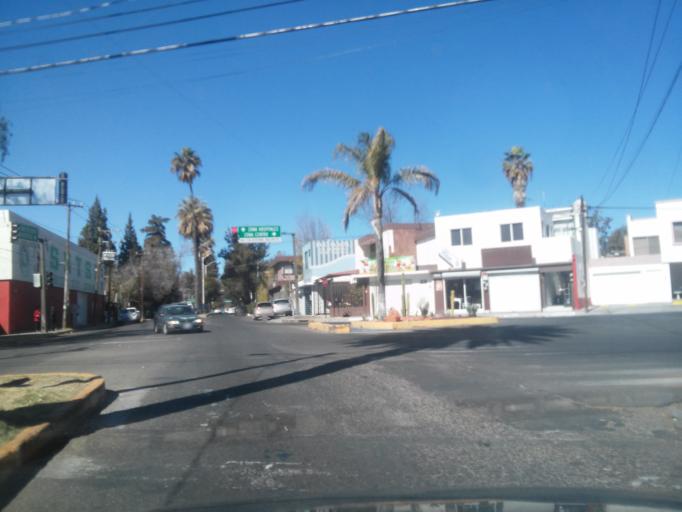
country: MX
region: Durango
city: Victoria de Durango
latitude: 24.0244
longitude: -104.6802
